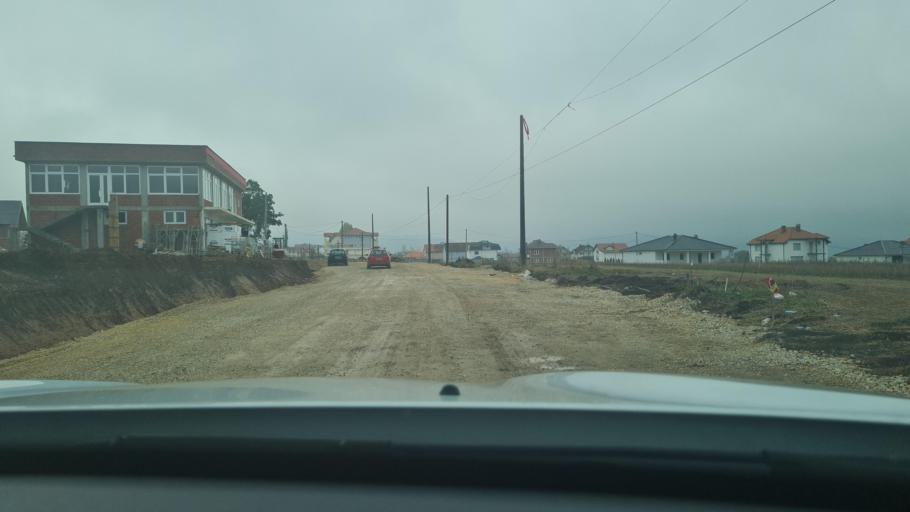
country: MK
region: Opstina Lipkovo
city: Matejche
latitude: 42.1165
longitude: 21.6073
